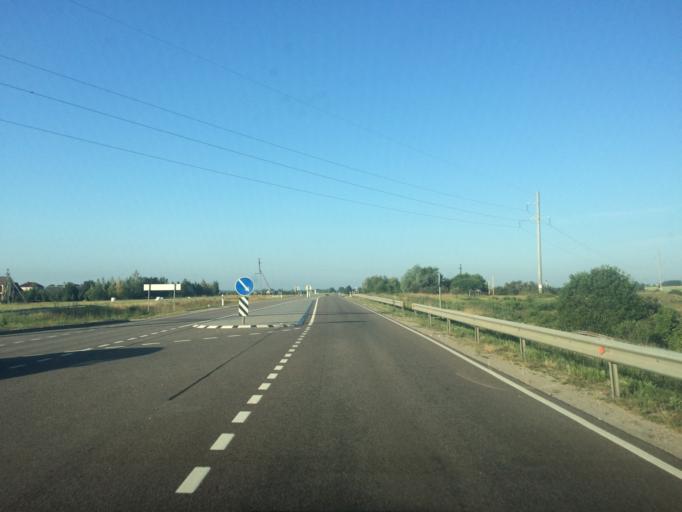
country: LT
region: Vilnius County
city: Ukmerge
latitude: 55.3238
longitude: 24.8791
